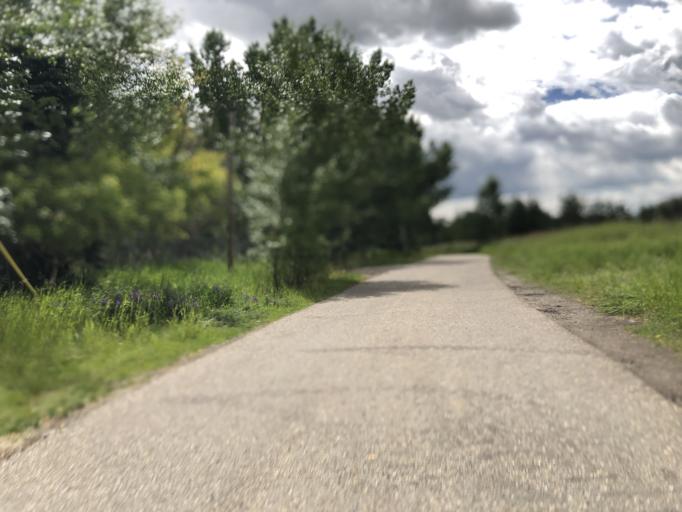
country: CA
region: Alberta
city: Calgary
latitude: 51.0274
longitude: -114.0112
